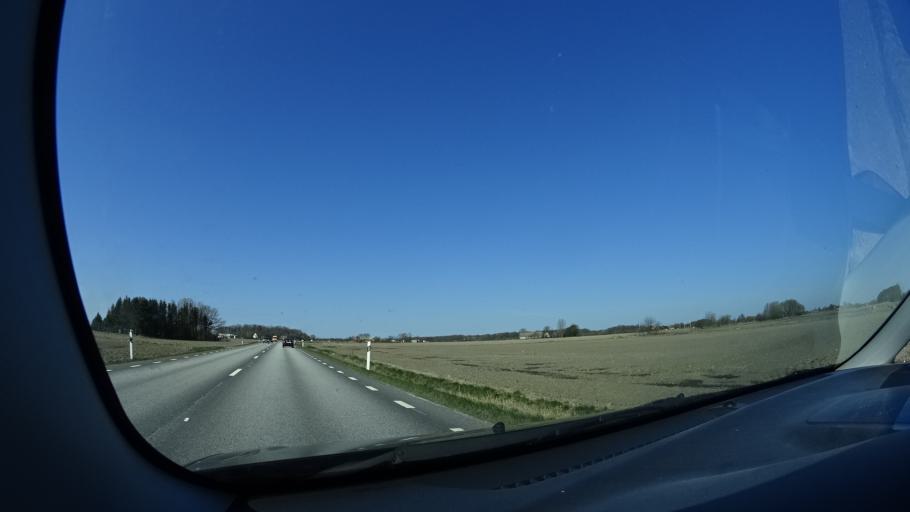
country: SE
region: Skane
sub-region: Angelholms Kommun
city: Strovelstorp
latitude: 56.2070
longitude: 12.7347
